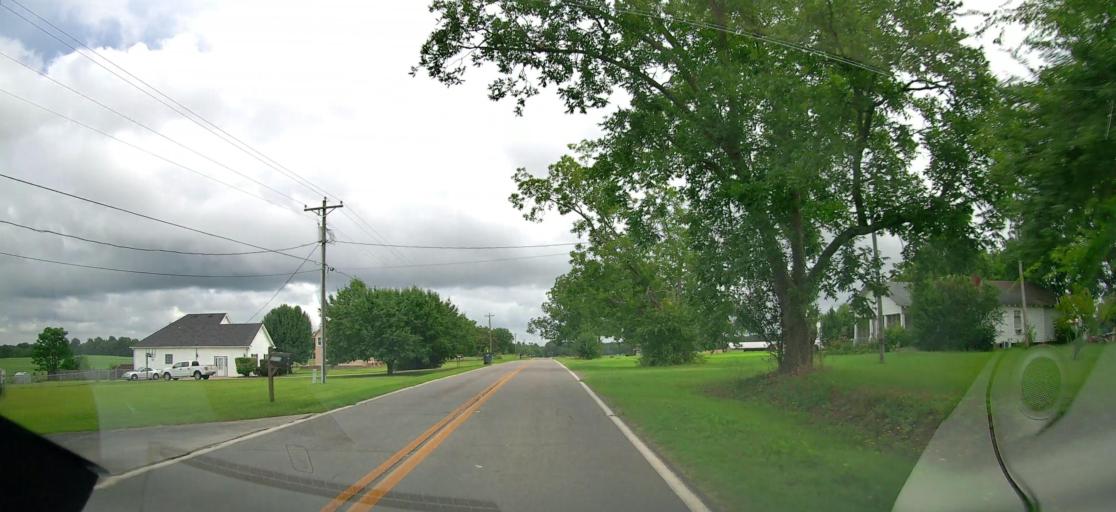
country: US
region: Georgia
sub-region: Bibb County
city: West Point
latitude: 32.7319
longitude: -83.7659
